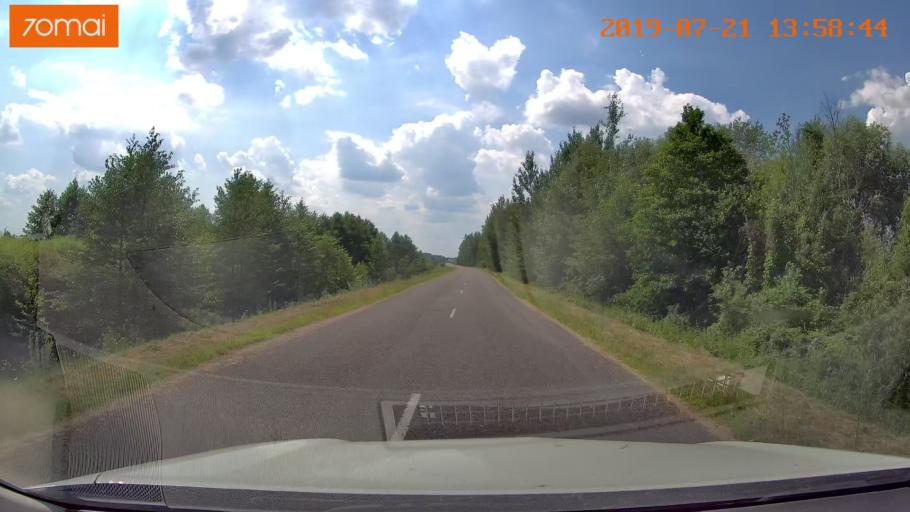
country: BY
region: Grodnenskaya
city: Lyubcha
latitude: 53.7587
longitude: 26.0739
